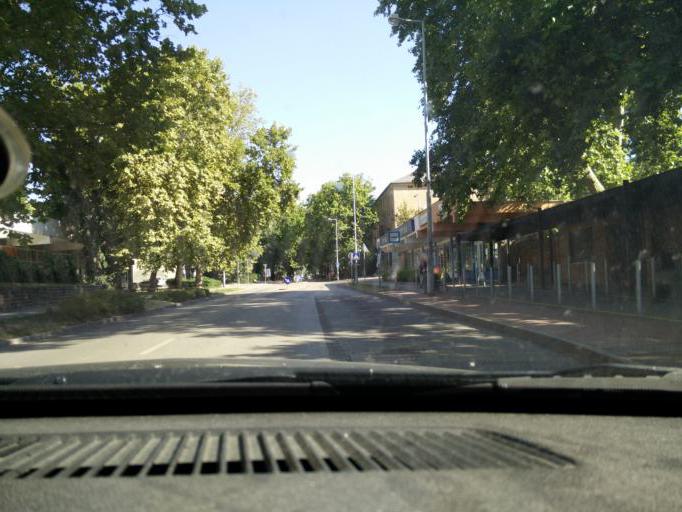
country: HU
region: Komarom-Esztergom
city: Tatabanya
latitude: 47.5907
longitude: 18.3946
